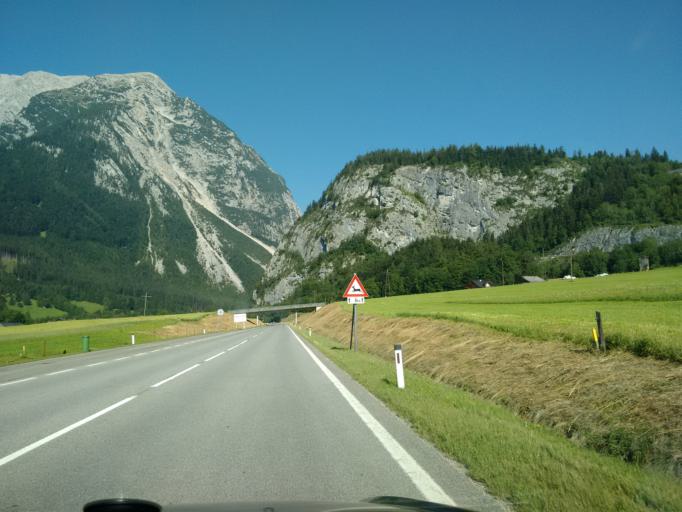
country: AT
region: Styria
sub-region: Politischer Bezirk Liezen
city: Irdning
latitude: 47.5254
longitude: 14.0704
